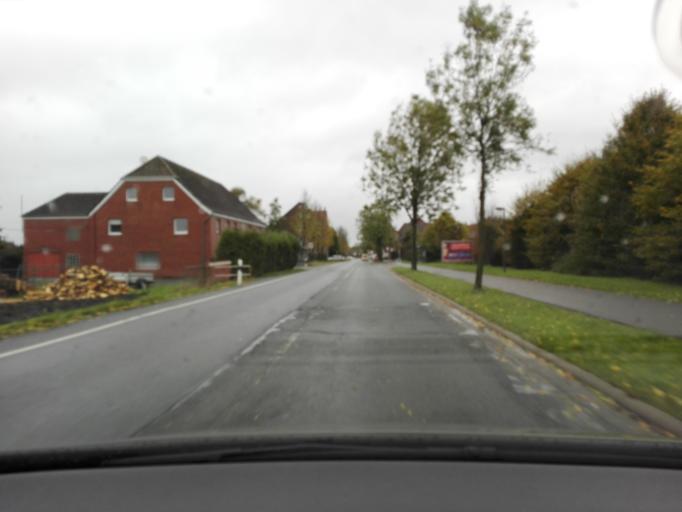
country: DE
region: North Rhine-Westphalia
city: Selm
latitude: 51.6790
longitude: 7.4706
